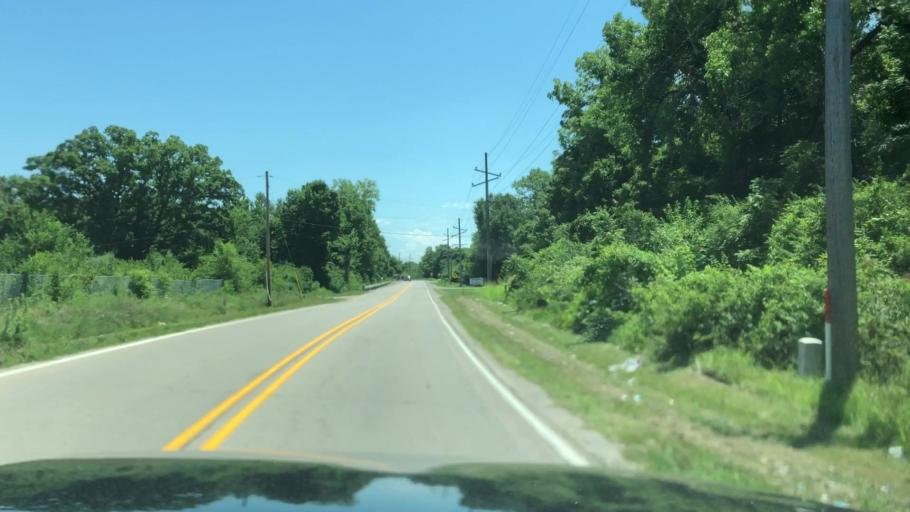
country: US
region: Illinois
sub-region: Saint Clair County
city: Alorton
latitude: 38.5515
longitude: -90.0750
